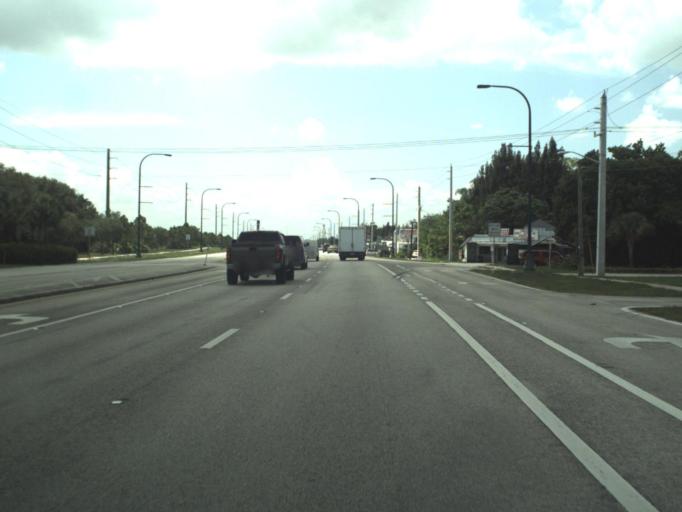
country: US
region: Florida
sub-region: Martin County
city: Hobe Sound
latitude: 27.0827
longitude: -80.1468
